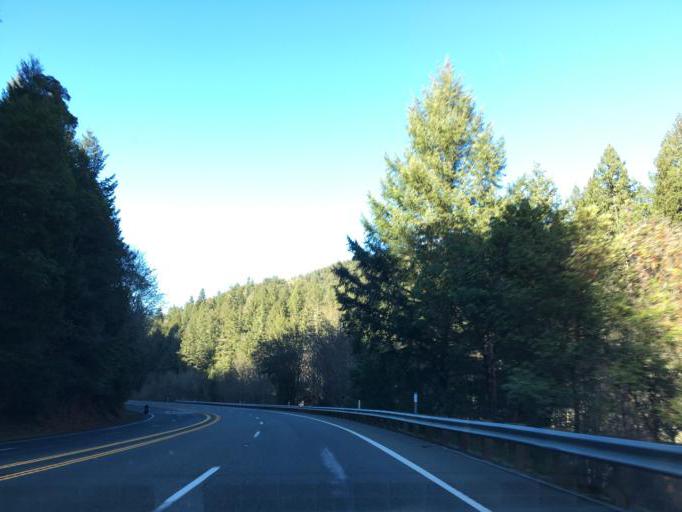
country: US
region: California
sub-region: Mendocino County
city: Laytonville
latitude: 39.5825
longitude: -123.4445
